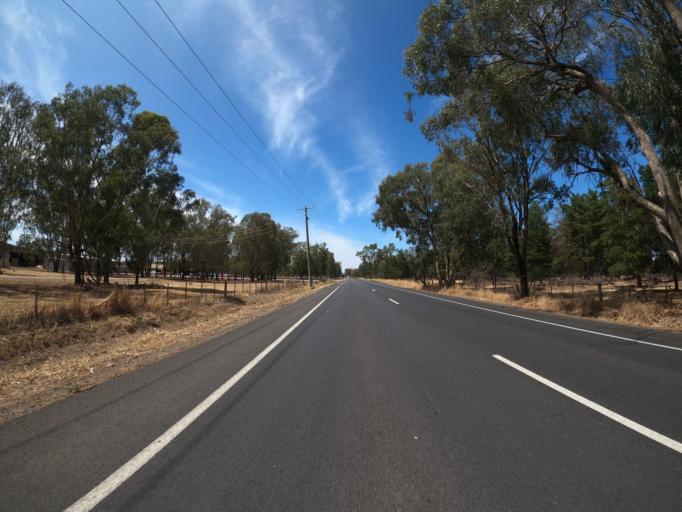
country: AU
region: Victoria
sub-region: Benalla
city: Benalla
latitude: -36.5257
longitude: 146.0383
